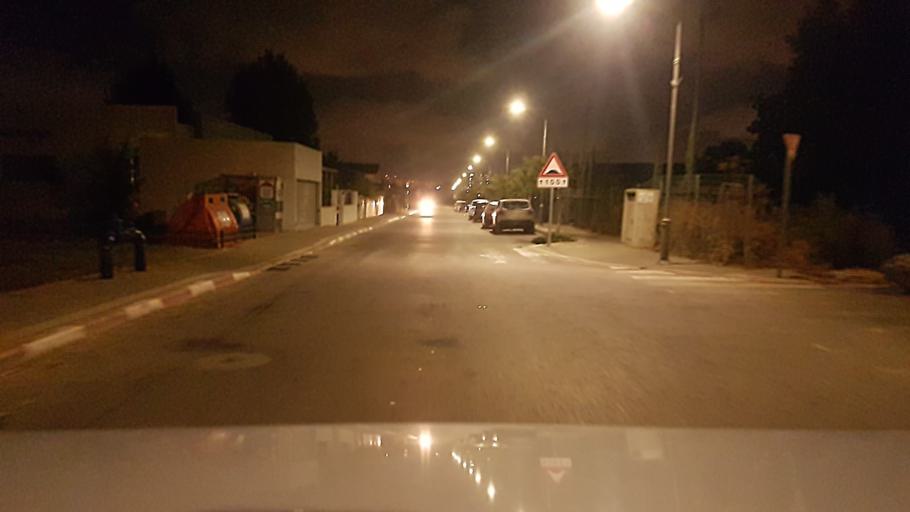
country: IL
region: Central District
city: Nehalim
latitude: 32.0731
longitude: 34.9198
